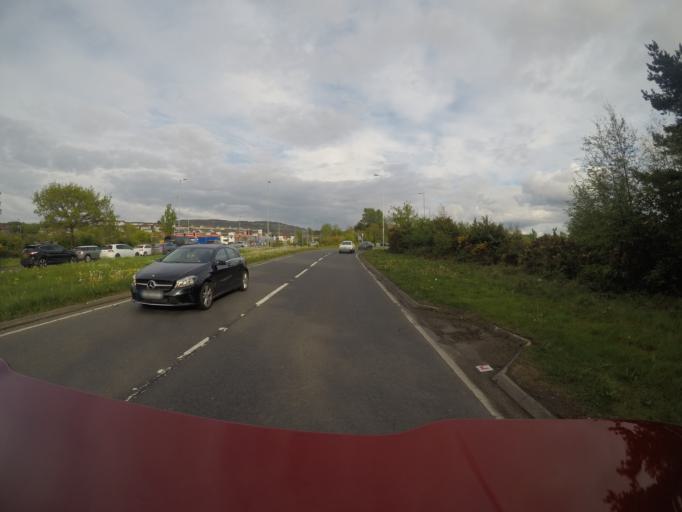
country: GB
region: Scotland
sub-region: West Dunbartonshire
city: Dumbarton
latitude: 55.9570
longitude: -4.5641
